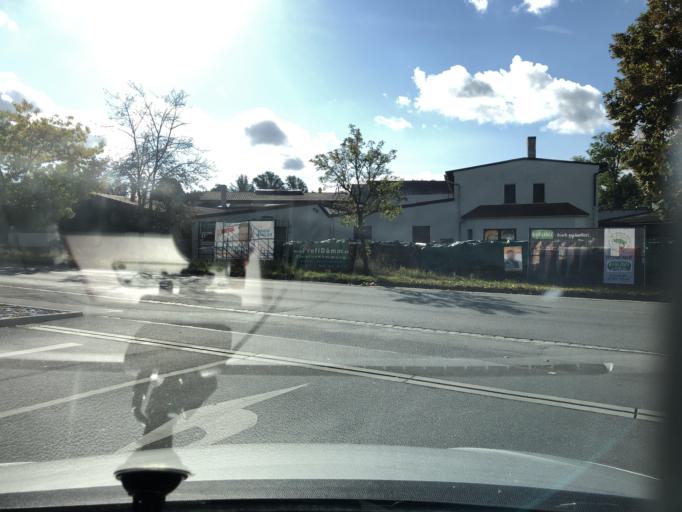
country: DE
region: Bavaria
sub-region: Regierungsbezirk Mittelfranken
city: Langenzenn
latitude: 49.4963
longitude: 10.8080
